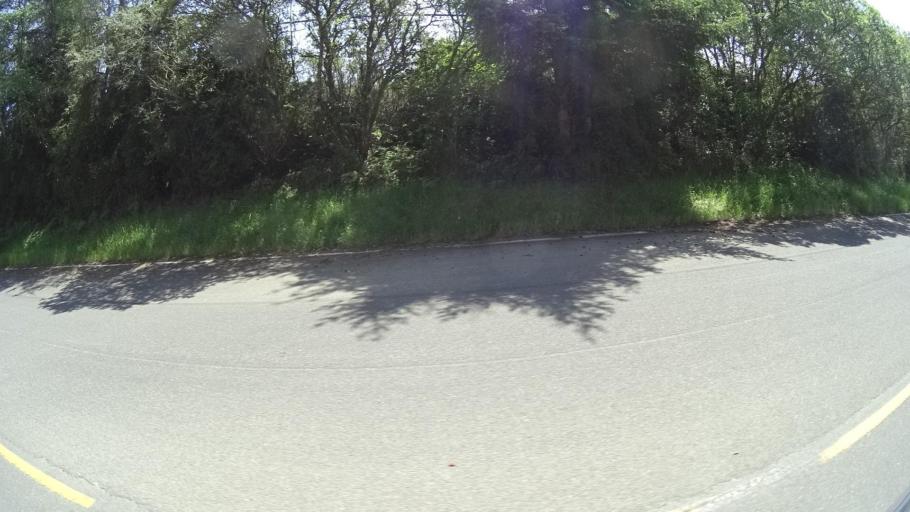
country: US
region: California
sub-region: Humboldt County
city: Humboldt Hill
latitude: 40.6507
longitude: -124.2236
